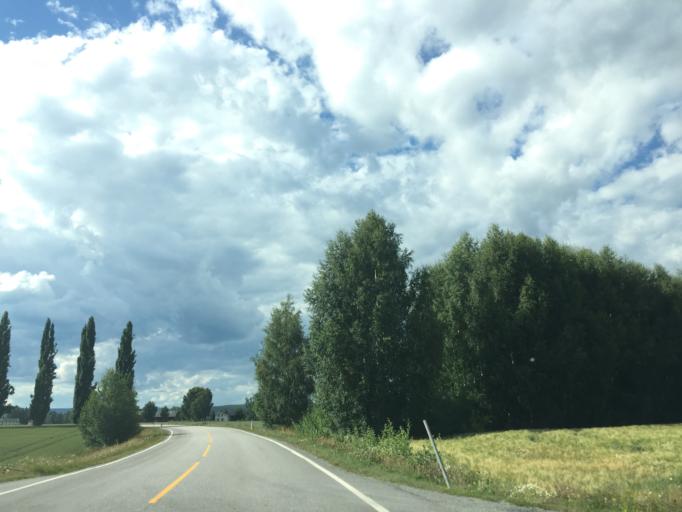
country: NO
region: Hedmark
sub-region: Sor-Odal
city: Skarnes
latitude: 60.2351
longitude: 11.7790
